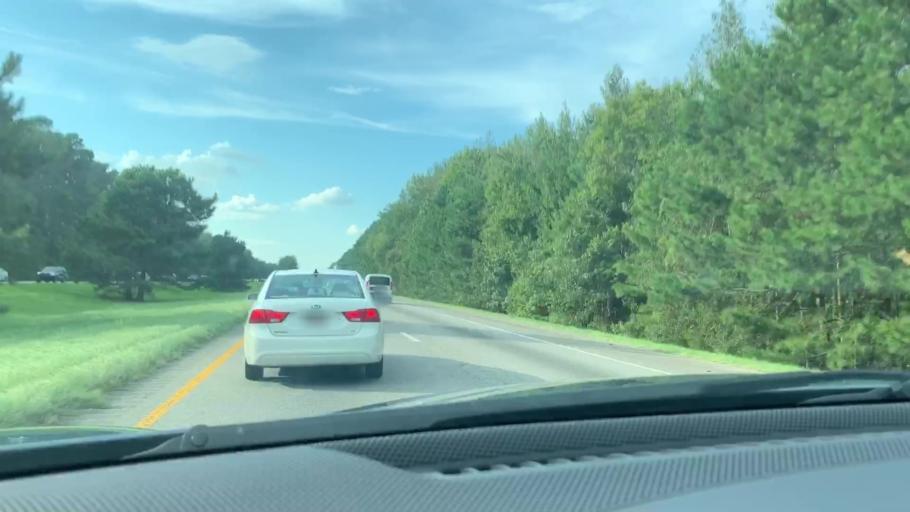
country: US
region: South Carolina
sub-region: Orangeburg County
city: Brookdale
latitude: 33.4285
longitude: -80.6888
